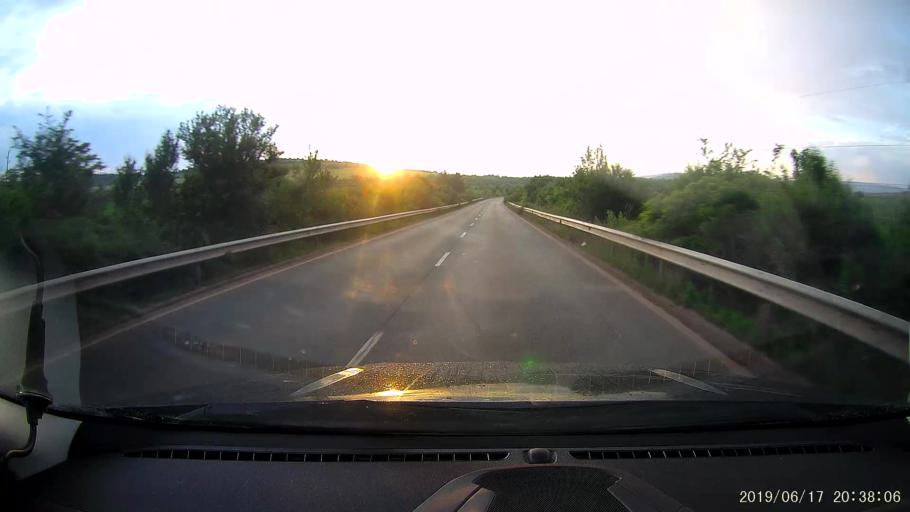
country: BG
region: Sofiya
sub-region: Obshtina Slivnitsa
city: Slivnitsa
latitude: 42.8683
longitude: 23.0223
